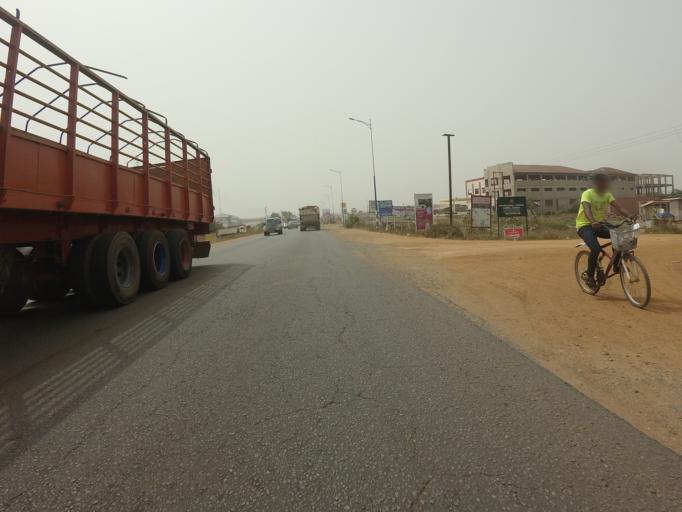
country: GH
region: Greater Accra
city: Tema
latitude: 5.7445
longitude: 0.0381
